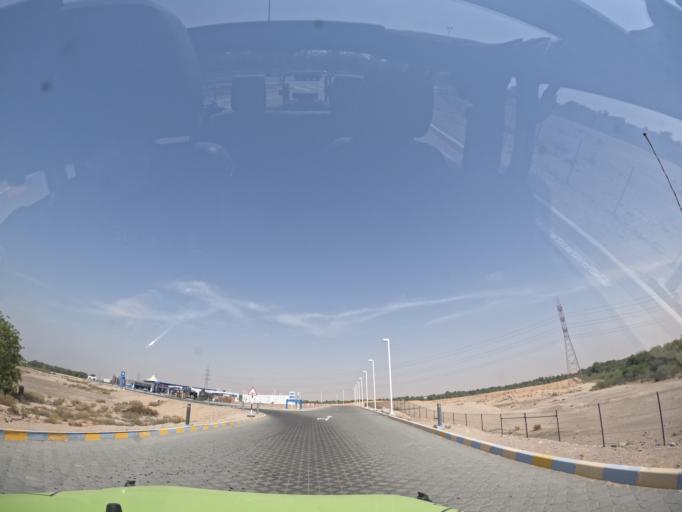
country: AE
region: Abu Dhabi
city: Al Ain
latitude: 24.1786
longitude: 55.1827
